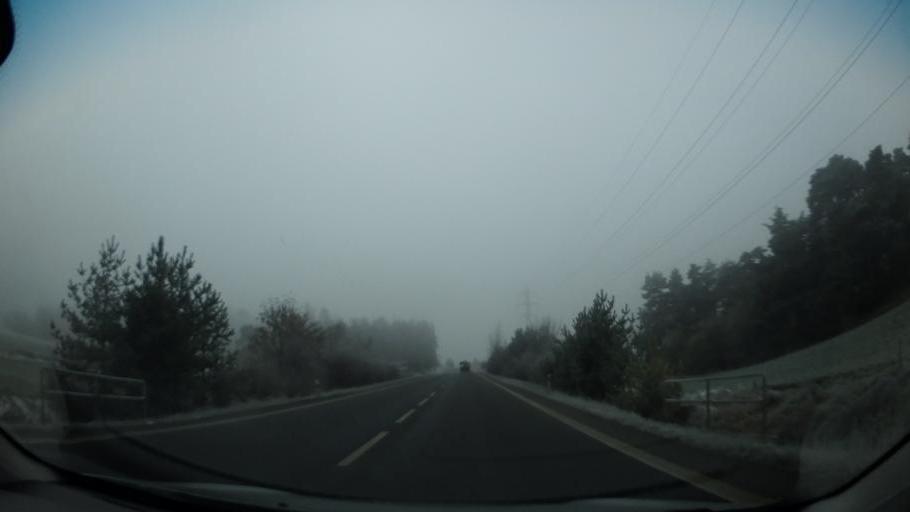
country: CZ
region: Vysocina
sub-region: Okres Trebic
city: Trebic
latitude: 49.2555
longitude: 15.9144
